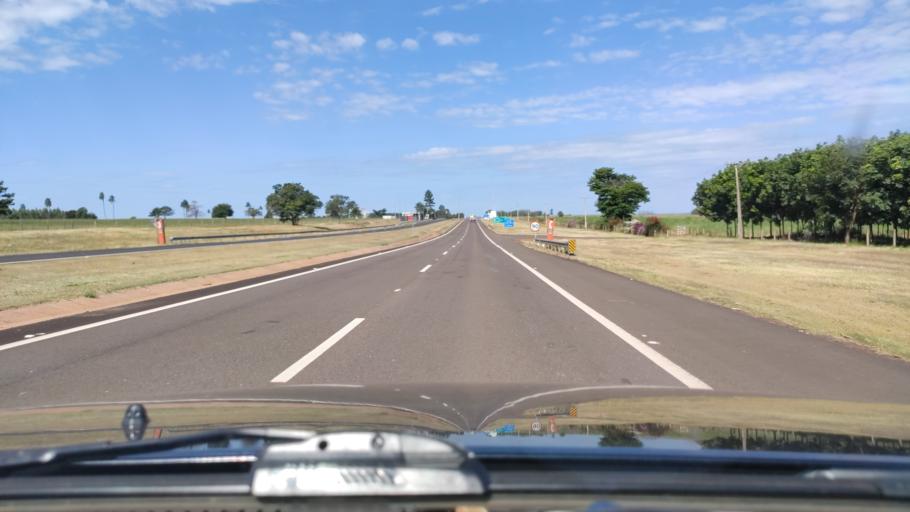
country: BR
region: Sao Paulo
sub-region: Rancharia
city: Rancharia
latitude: -22.4472
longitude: -50.9881
